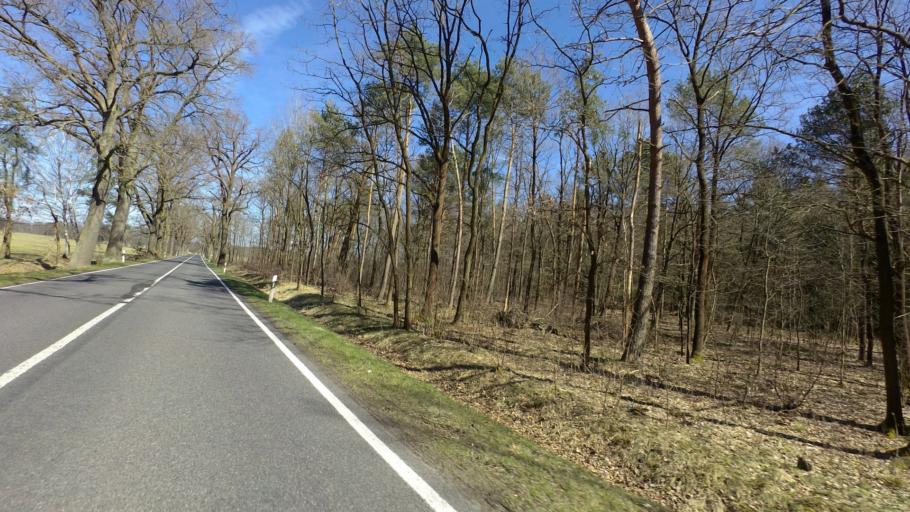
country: DE
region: Brandenburg
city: Munchehofe
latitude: 52.1346
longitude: 13.8268
